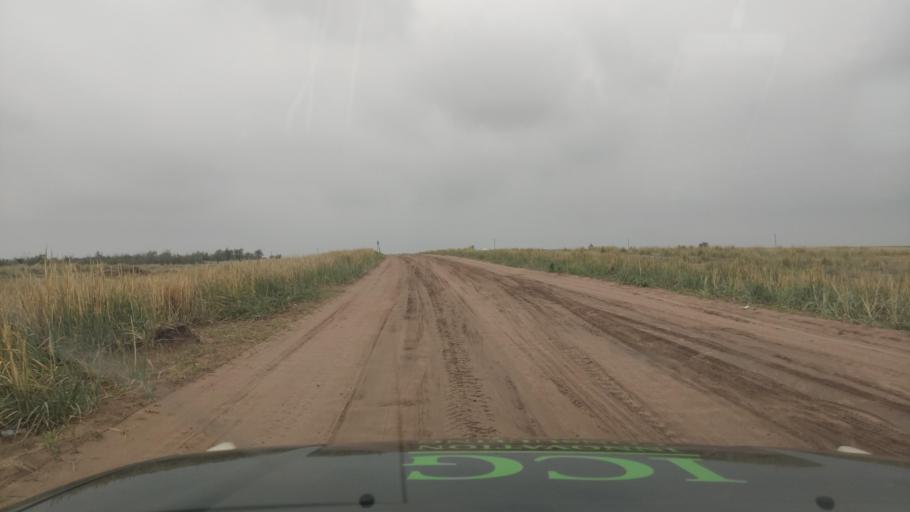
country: KZ
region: Pavlodar
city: Aksu
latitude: 52.0589
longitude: 77.1520
